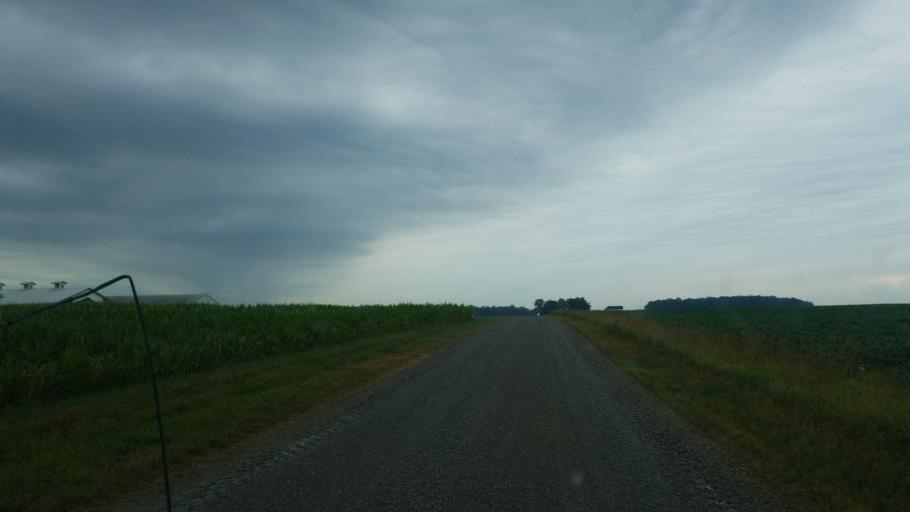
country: US
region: Indiana
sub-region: DeKalb County
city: Butler
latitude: 41.4669
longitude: -84.9104
